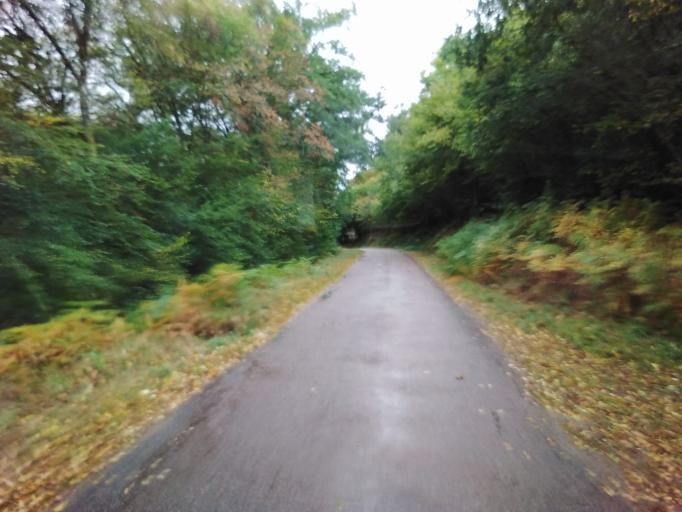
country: FR
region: Bourgogne
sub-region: Departement de la Nievre
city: Lormes
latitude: 47.3395
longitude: 3.9195
